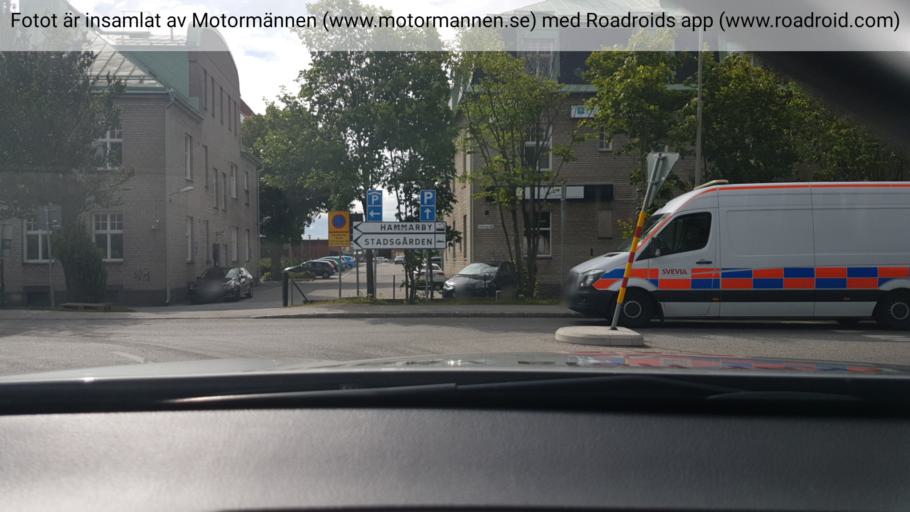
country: SE
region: Stockholm
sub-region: Stockholms Kommun
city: Arsta
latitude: 59.2931
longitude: 18.0728
